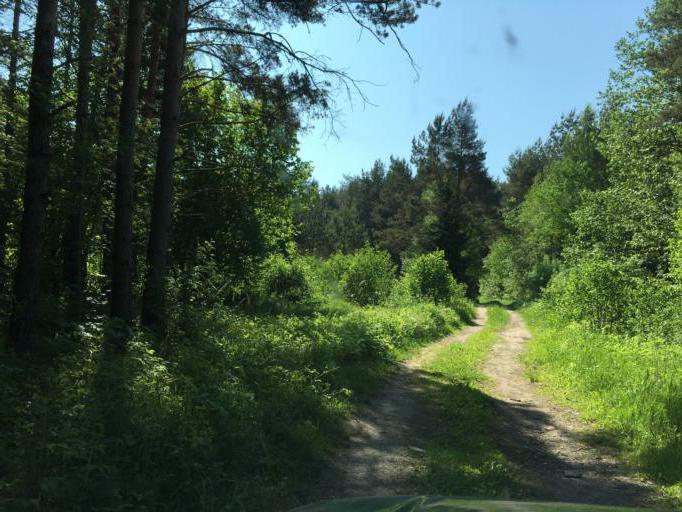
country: LV
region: Ventspils
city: Ventspils
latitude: 57.4757
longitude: 21.7643
